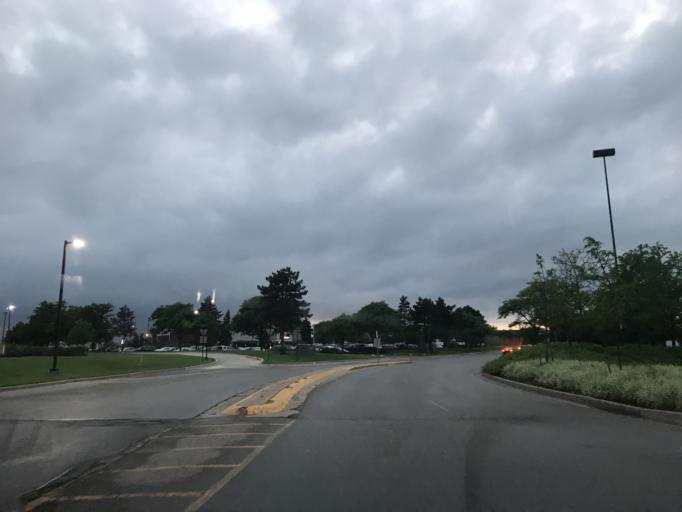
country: US
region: Michigan
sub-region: Oakland County
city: Novi
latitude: 42.4896
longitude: -83.4735
